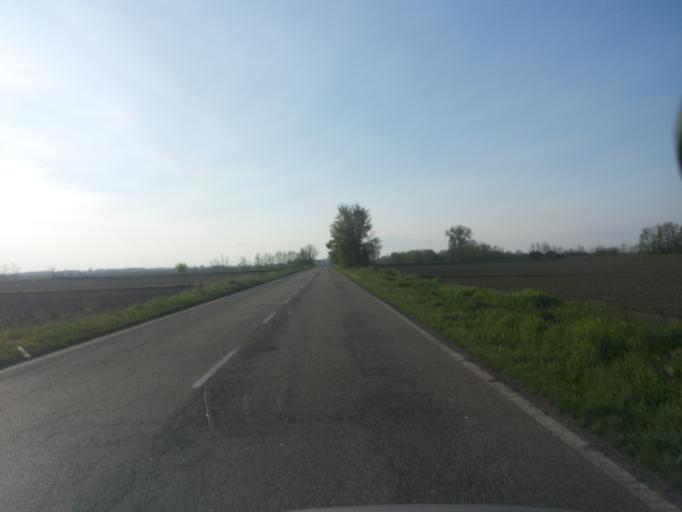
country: IT
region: Lombardy
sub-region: Provincia di Pavia
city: Candia Lomellina
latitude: 45.1983
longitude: 8.5852
